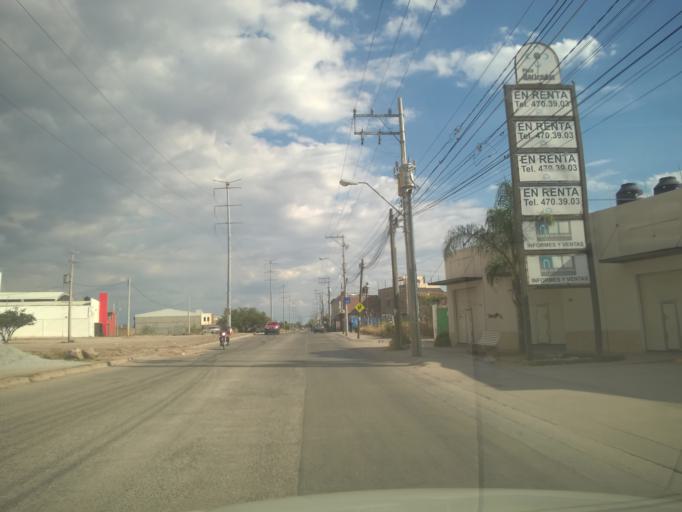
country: MX
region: Guanajuato
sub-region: Leon
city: Fraccionamiento Paraiso Real
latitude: 21.0746
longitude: -101.6153
